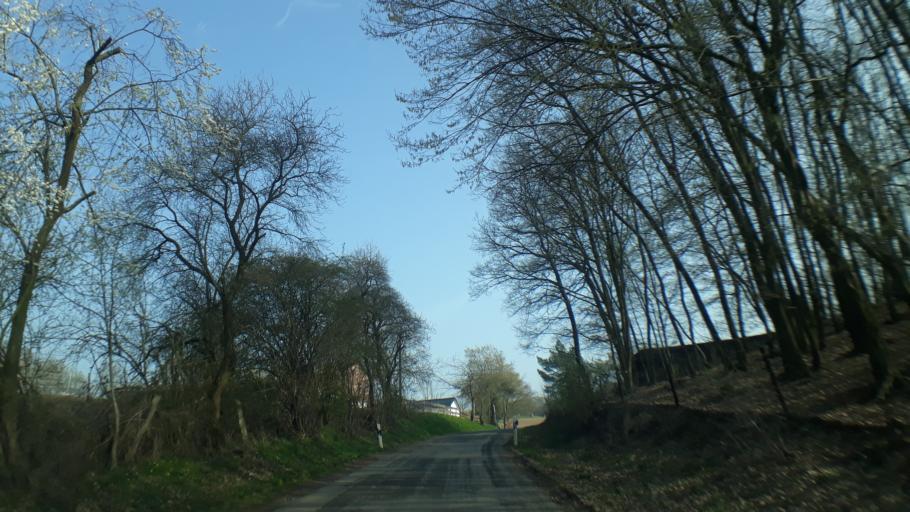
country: DE
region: North Rhine-Westphalia
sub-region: Regierungsbezirk Koln
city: Bad Munstereifel
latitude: 50.5414
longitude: 6.7289
